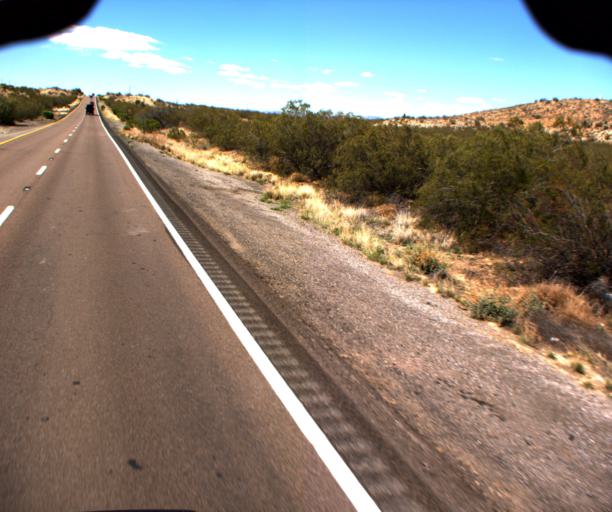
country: US
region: Arizona
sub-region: Mohave County
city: Kingman
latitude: 35.0218
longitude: -113.6641
